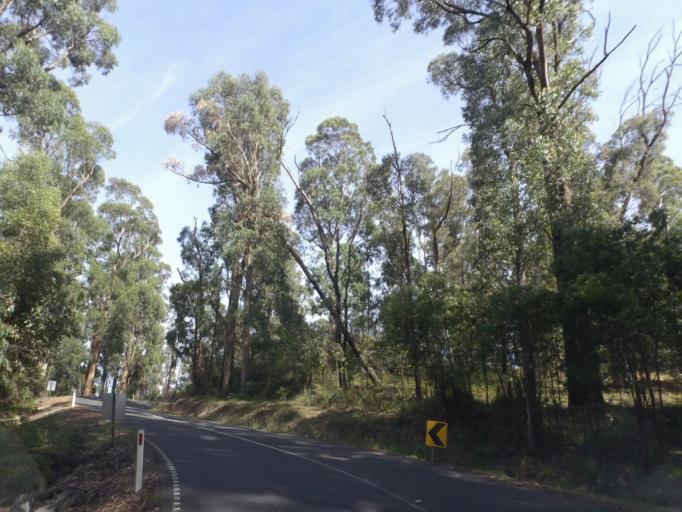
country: AU
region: Victoria
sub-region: Nillumbik
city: Saint Andrews
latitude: -37.5404
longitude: 145.3389
